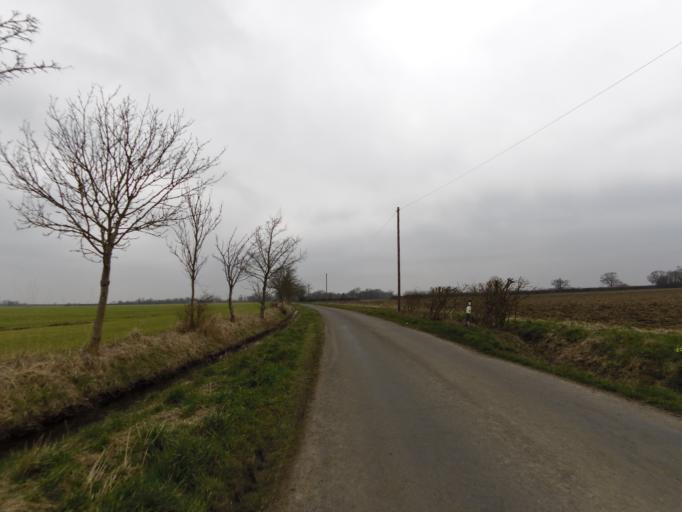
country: GB
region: England
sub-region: Suffolk
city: Framlingham
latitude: 52.2357
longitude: 1.3758
